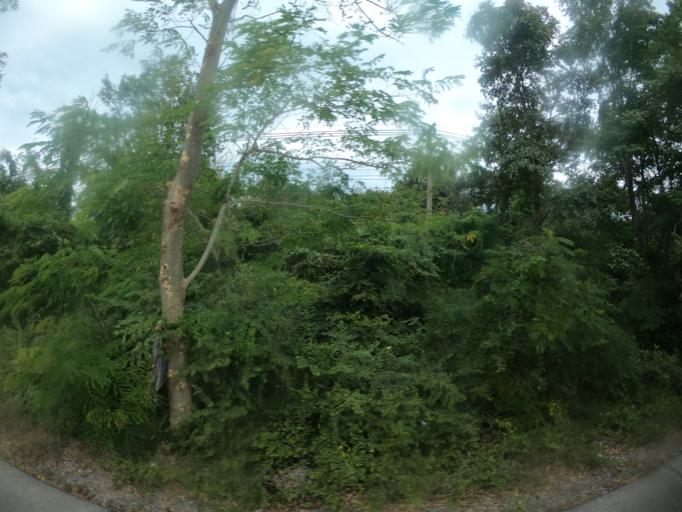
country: TH
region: Maha Sarakham
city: Kantharawichai
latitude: 16.3376
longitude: 103.2215
